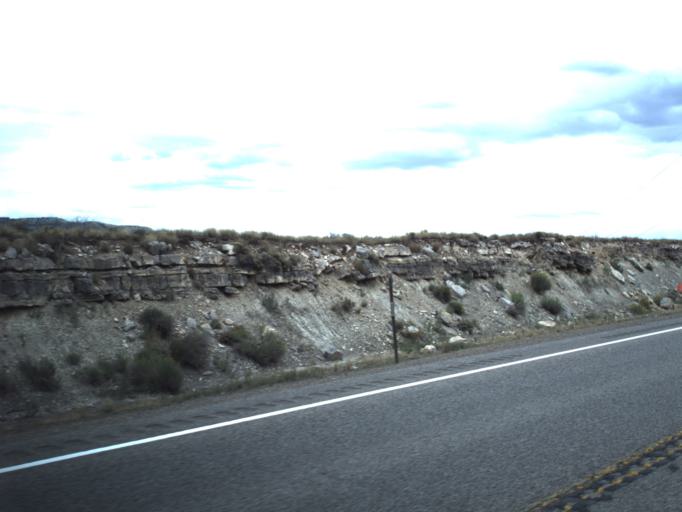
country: US
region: Utah
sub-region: Carbon County
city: Helper
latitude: 39.8232
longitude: -110.9464
